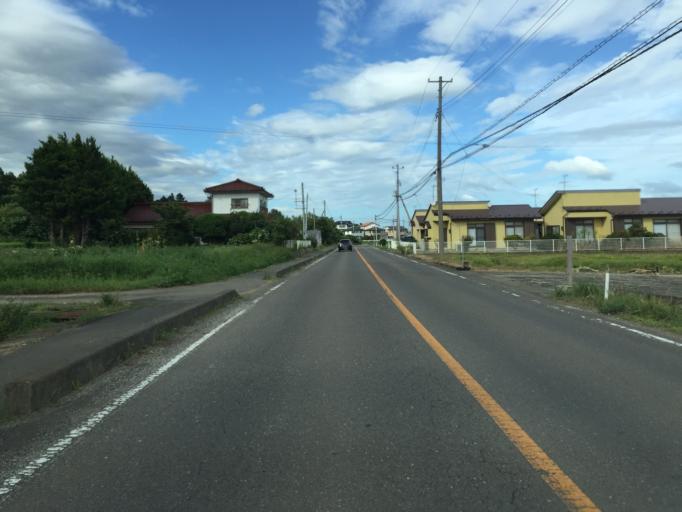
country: JP
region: Fukushima
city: Motomiya
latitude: 37.5402
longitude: 140.3753
